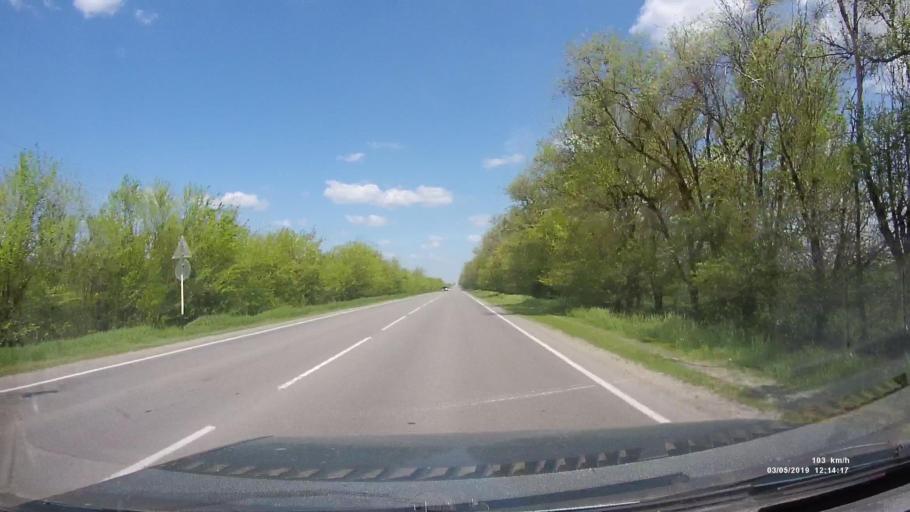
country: RU
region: Rostov
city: Melikhovskaya
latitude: 47.3419
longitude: 40.5618
